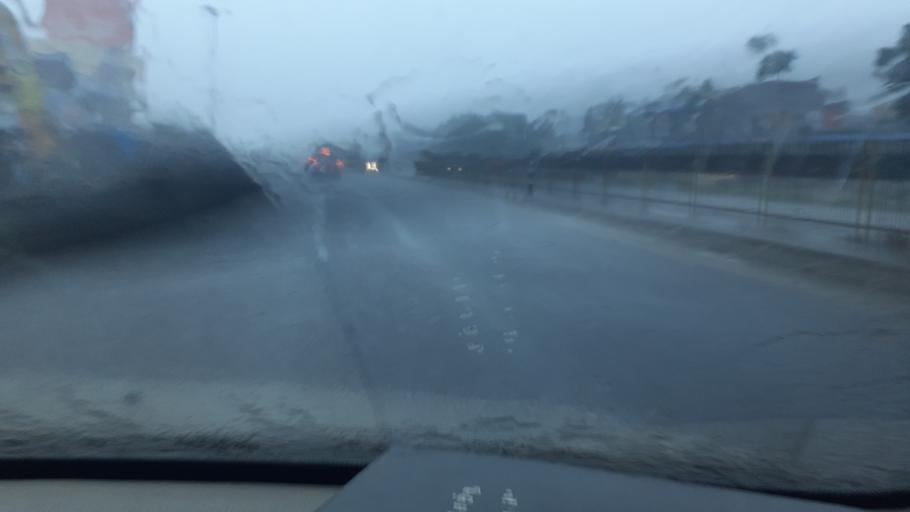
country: IN
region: Tamil Nadu
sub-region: Virudhunagar
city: Tiruttangal
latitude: 9.4619
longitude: 77.9329
